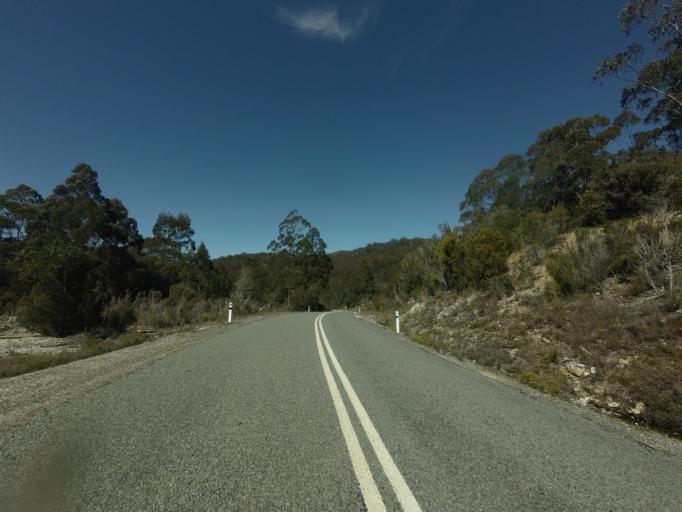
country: AU
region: Tasmania
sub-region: Derwent Valley
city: New Norfolk
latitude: -42.7584
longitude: 146.4014
